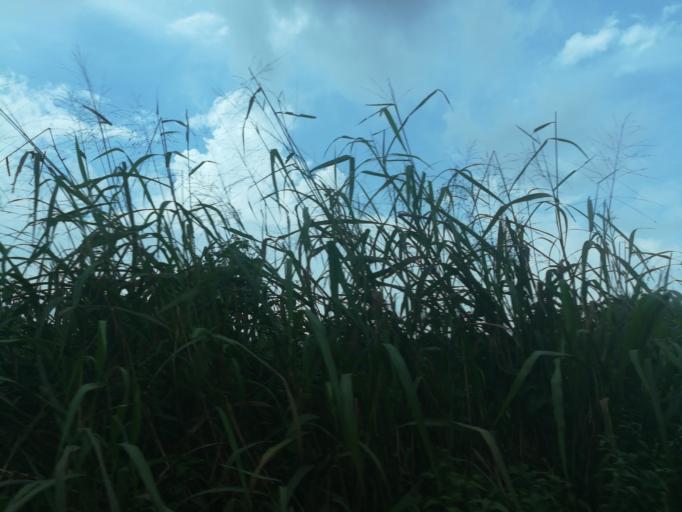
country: NG
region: Lagos
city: Ikorodu
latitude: 6.6632
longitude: 3.6314
